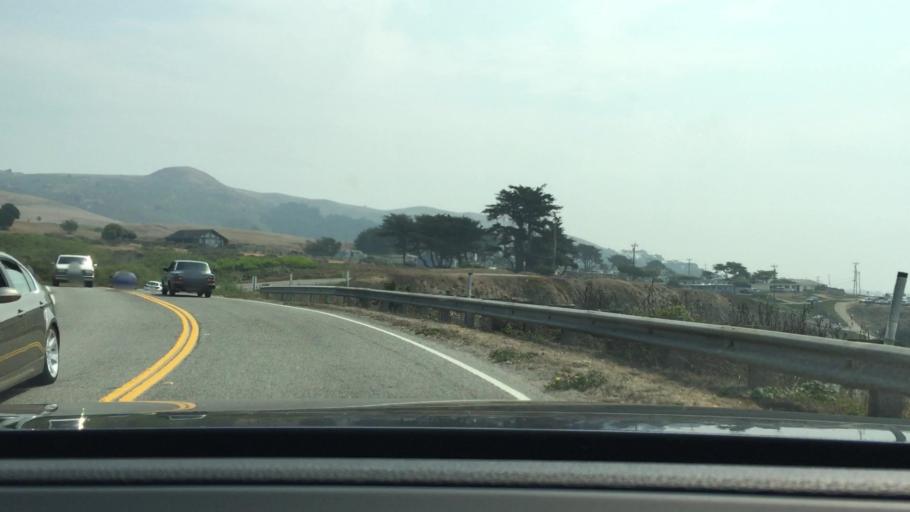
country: US
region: California
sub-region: Sonoma County
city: Bodega Bay
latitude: 38.3776
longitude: -123.0796
